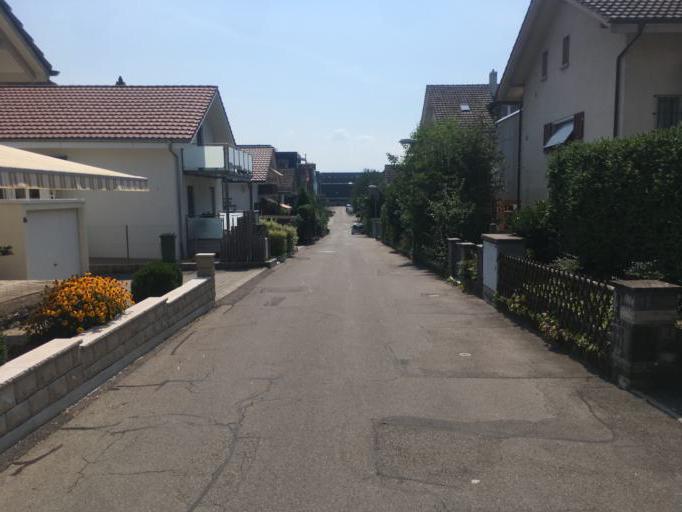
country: CH
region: Bern
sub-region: Bern-Mittelland District
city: Muri
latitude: 46.9382
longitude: 7.4974
